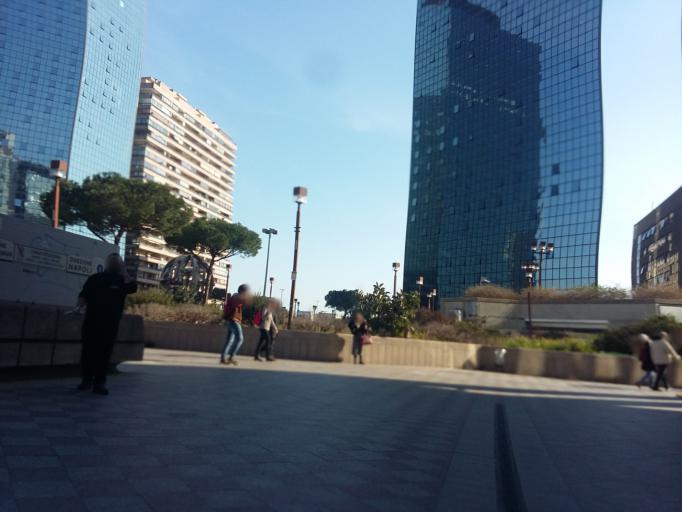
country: IT
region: Campania
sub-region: Provincia di Napoli
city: Napoli
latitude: 40.8574
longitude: 14.2816
